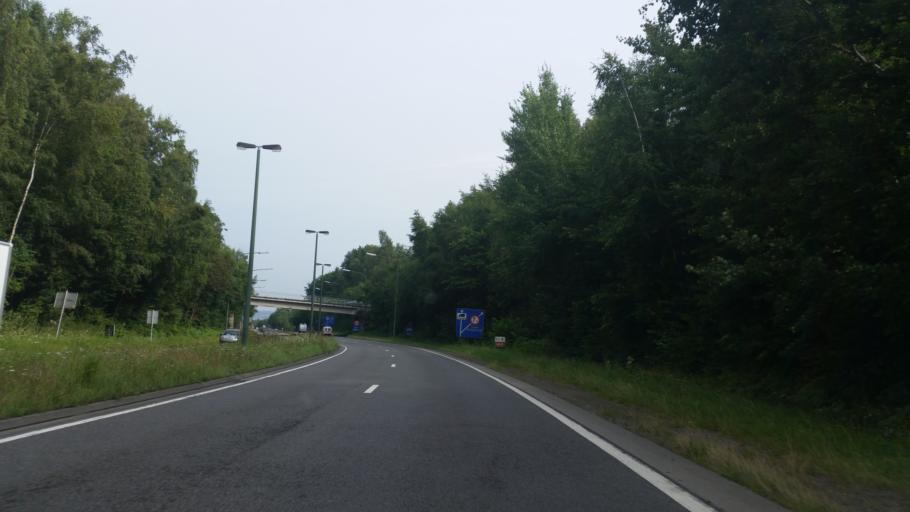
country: BE
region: Wallonia
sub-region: Province de Liege
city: Esneux
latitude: 50.5771
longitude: 5.5537
